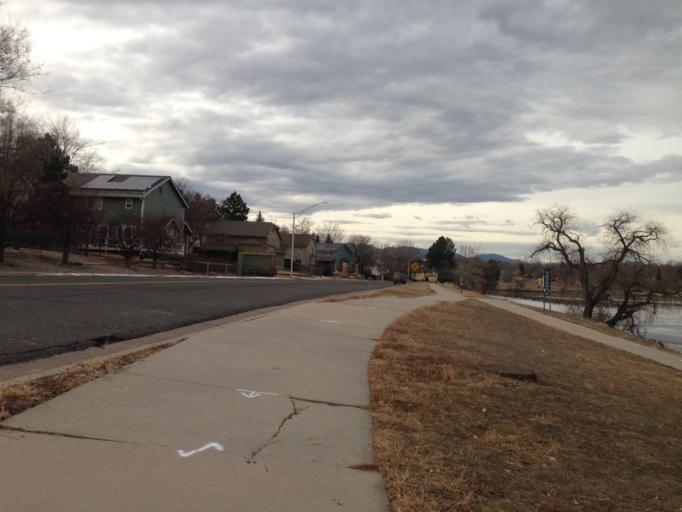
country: US
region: Colorado
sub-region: Adams County
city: Westminster
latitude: 39.8425
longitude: -105.0683
